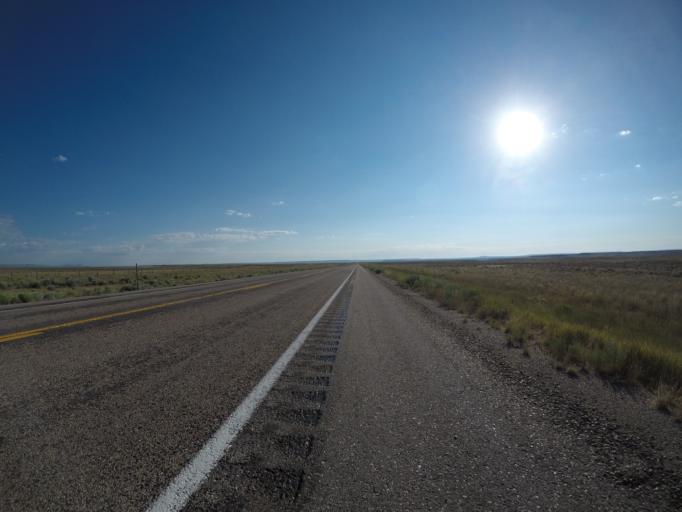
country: US
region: Wyoming
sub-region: Lincoln County
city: Kemmerer
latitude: 41.9235
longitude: -110.2862
